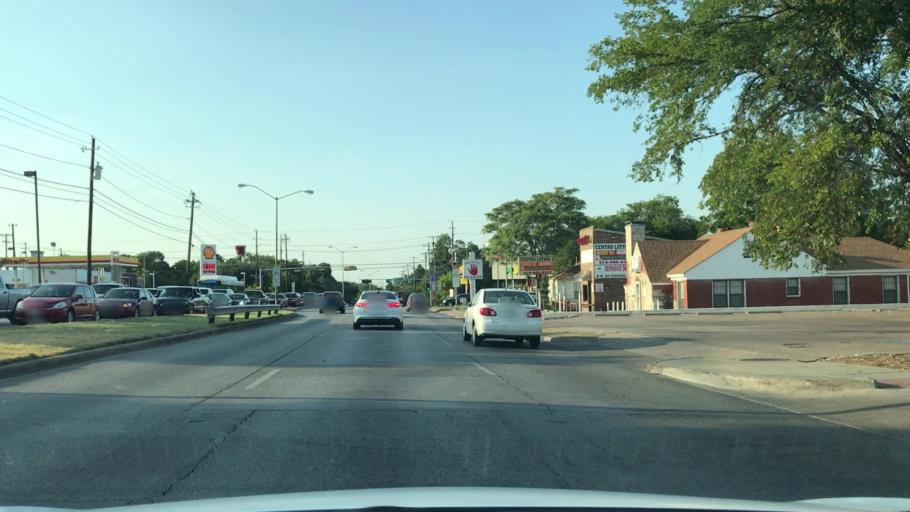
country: US
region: Texas
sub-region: Dallas County
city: Cockrell Hill
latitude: 32.7481
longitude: -96.8567
